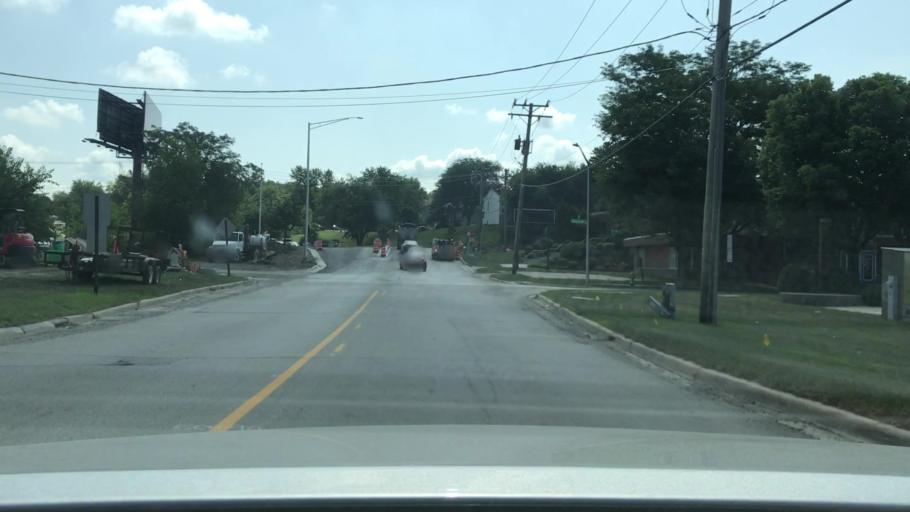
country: US
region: Illinois
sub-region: Will County
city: Bolingbrook
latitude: 41.7180
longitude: -88.0702
